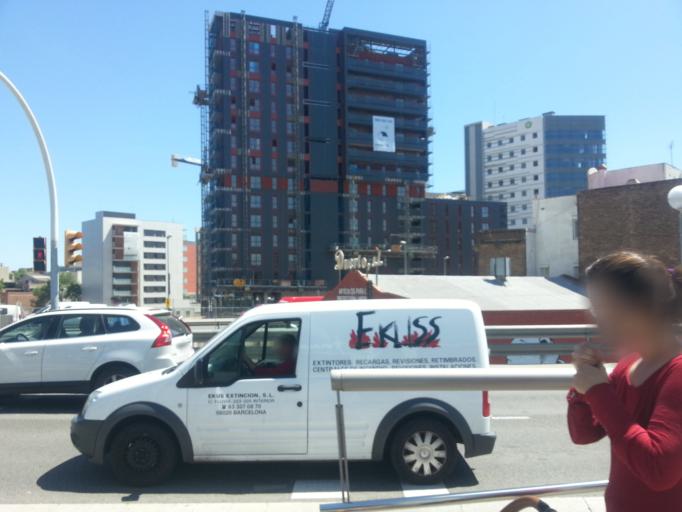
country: ES
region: Catalonia
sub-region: Provincia de Barcelona
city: Ciutat Vella
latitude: 41.3977
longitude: 2.1871
